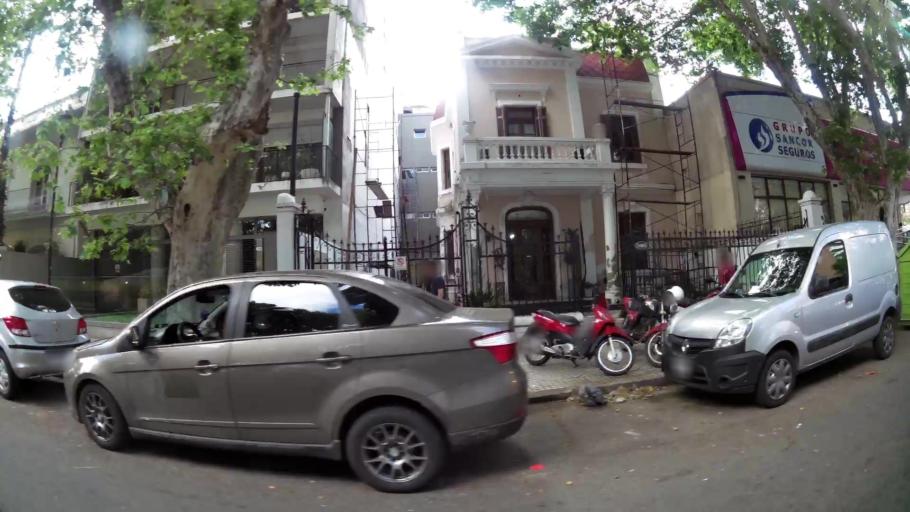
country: AR
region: Santa Fe
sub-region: Departamento de Rosario
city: Rosario
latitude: -32.9472
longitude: -60.6540
